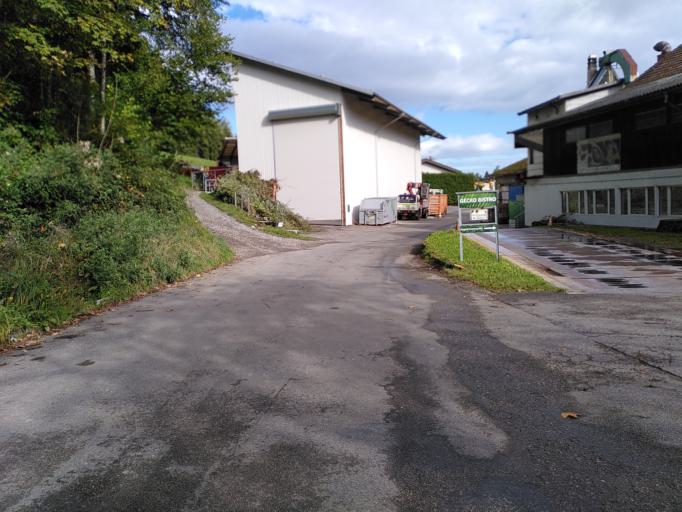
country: CH
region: Bern
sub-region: Oberaargau
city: Seeberg
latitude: 47.1436
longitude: 7.6945
